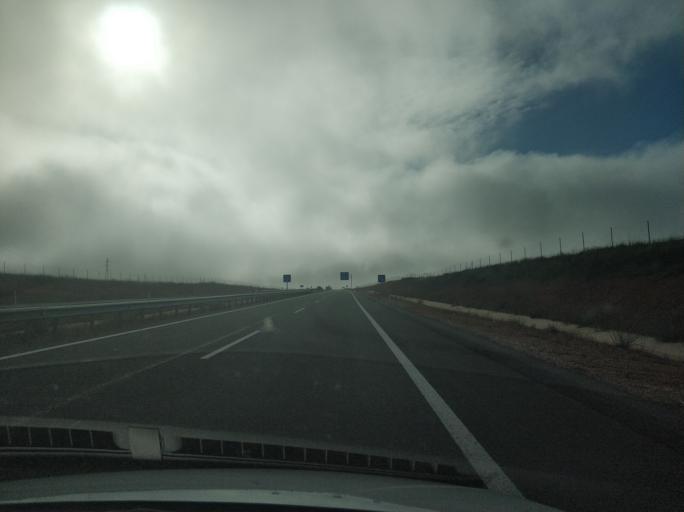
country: ES
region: Castille and Leon
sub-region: Provincia de Soria
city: Alcubilla de las Penas
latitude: 41.2743
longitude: -2.4748
